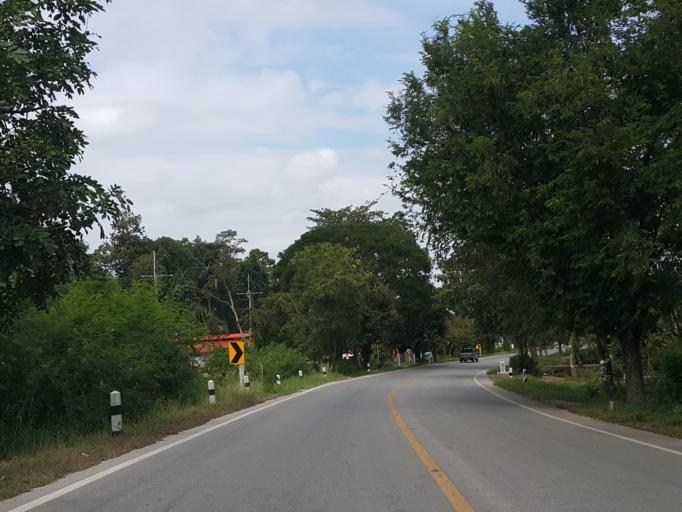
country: TH
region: Lampang
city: Lampang
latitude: 18.3430
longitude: 99.4588
